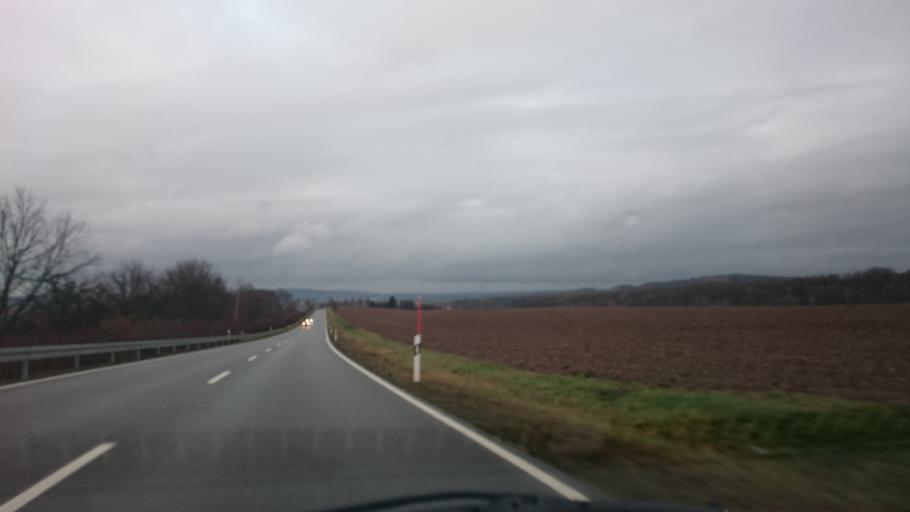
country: DE
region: Saxony
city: Lichtenstein
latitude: 50.7582
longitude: 12.6048
